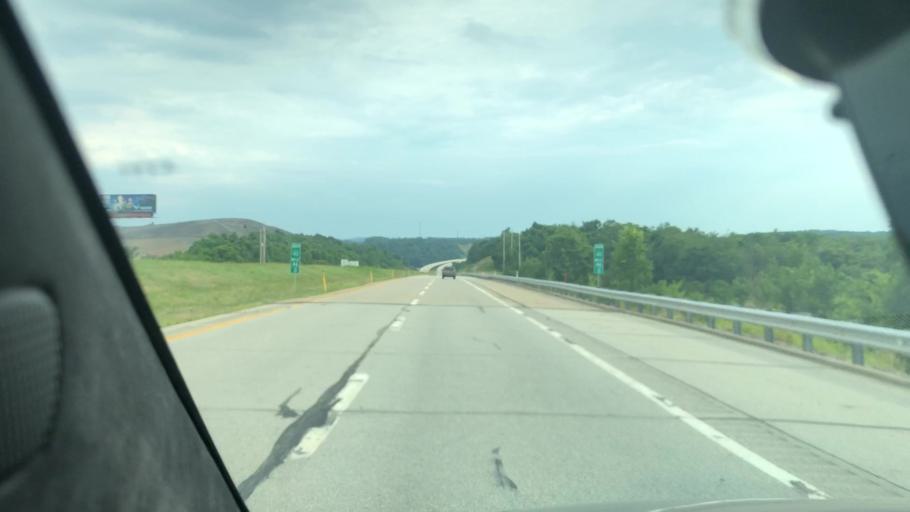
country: US
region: Pennsylvania
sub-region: Washington County
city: Baidland
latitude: 40.2244
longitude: -79.9856
